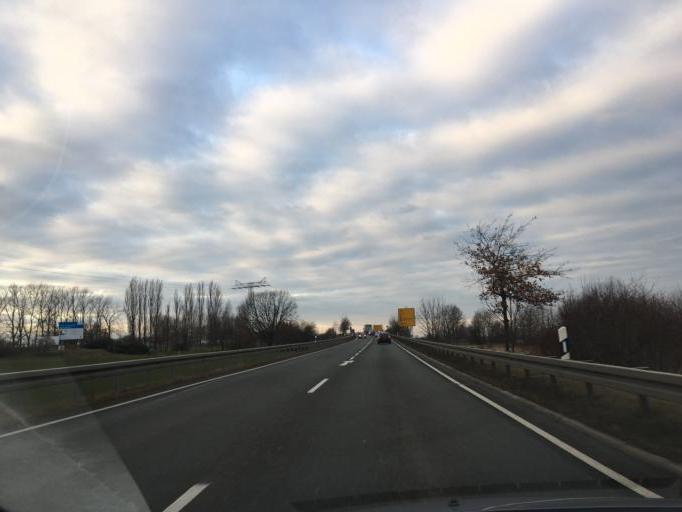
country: DE
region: Thuringia
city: Altenburg
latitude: 51.0066
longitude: 12.4602
